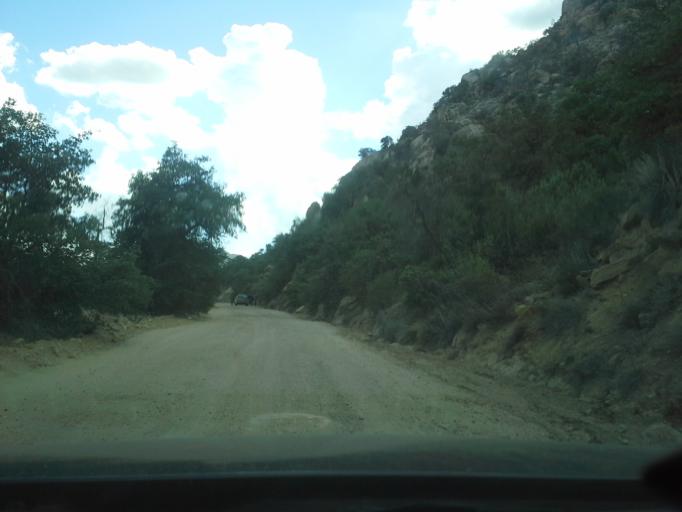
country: US
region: Arizona
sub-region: Yavapai County
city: Mayer
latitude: 34.2318
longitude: -112.3092
